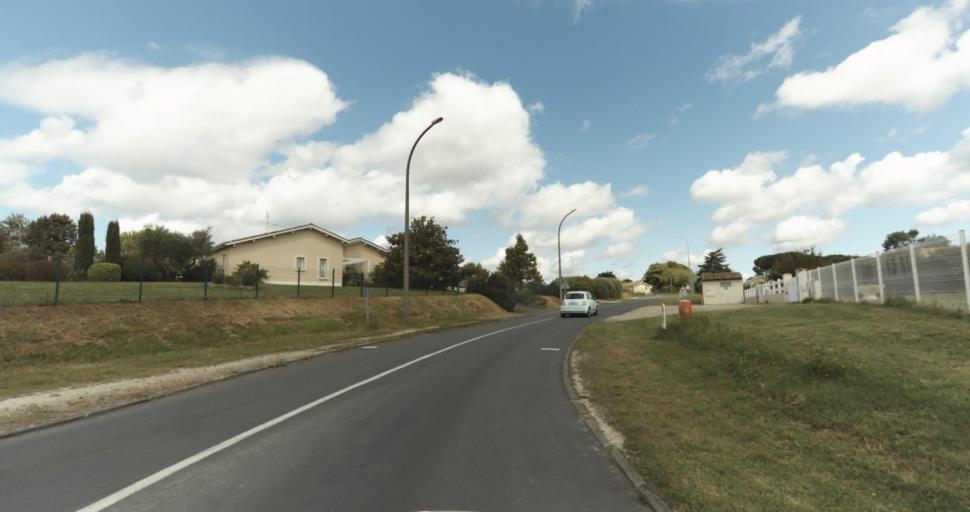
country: FR
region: Aquitaine
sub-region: Departement de la Gironde
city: Bazas
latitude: 44.4370
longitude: -0.2069
